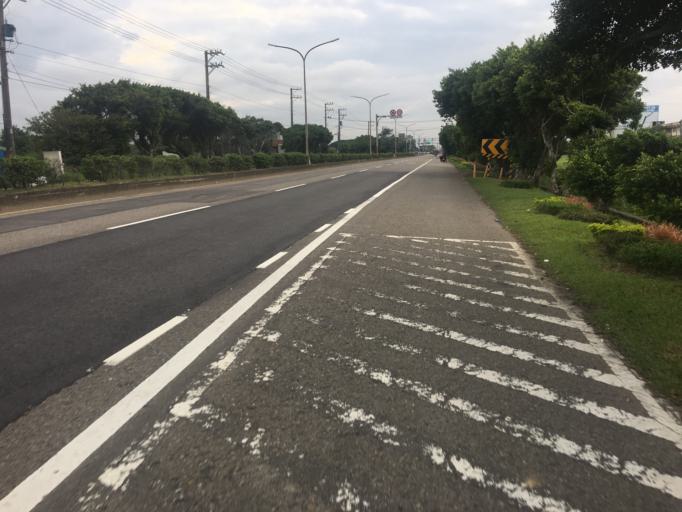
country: TW
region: Taiwan
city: Taoyuan City
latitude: 25.0930
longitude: 121.2321
